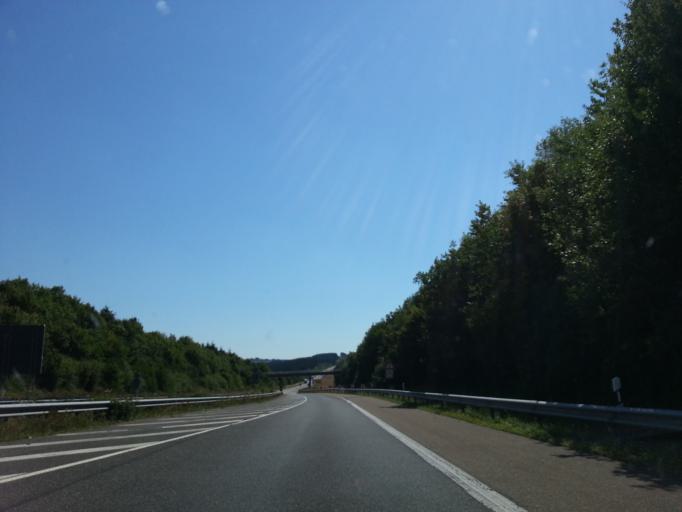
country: DE
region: Rheinland-Pfalz
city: Winterspelt
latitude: 50.2240
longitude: 6.2060
